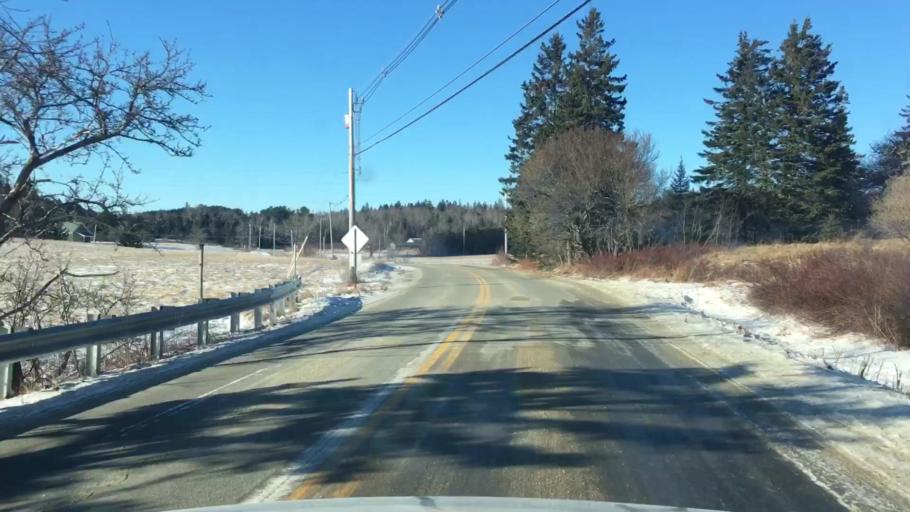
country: US
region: Maine
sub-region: Hancock County
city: Castine
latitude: 44.3500
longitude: -68.7490
